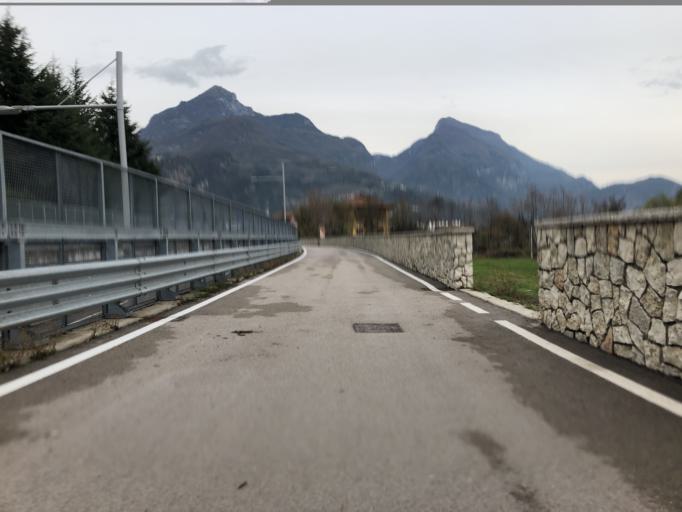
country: IT
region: Trentino-Alto Adige
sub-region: Provincia di Trento
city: Riva del Garda
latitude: 45.8944
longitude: 10.8385
